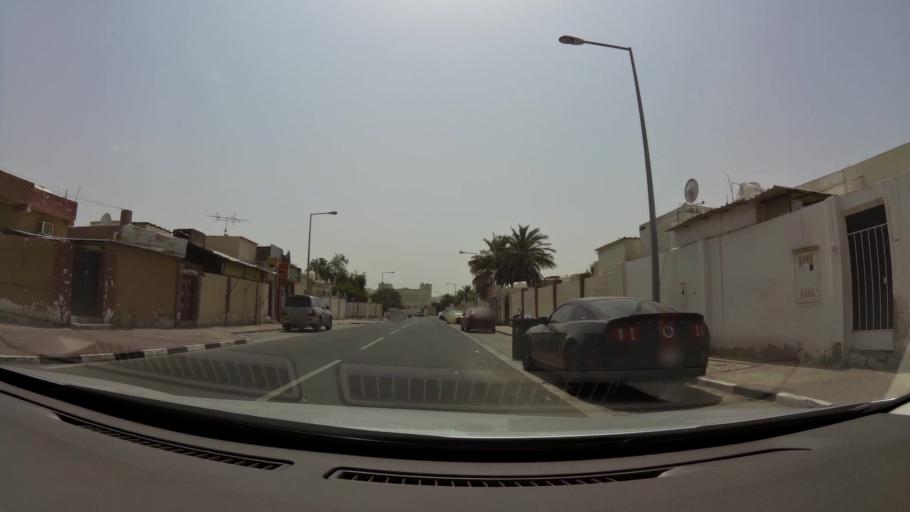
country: QA
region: Baladiyat ad Dawhah
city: Doha
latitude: 25.3161
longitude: 51.4790
